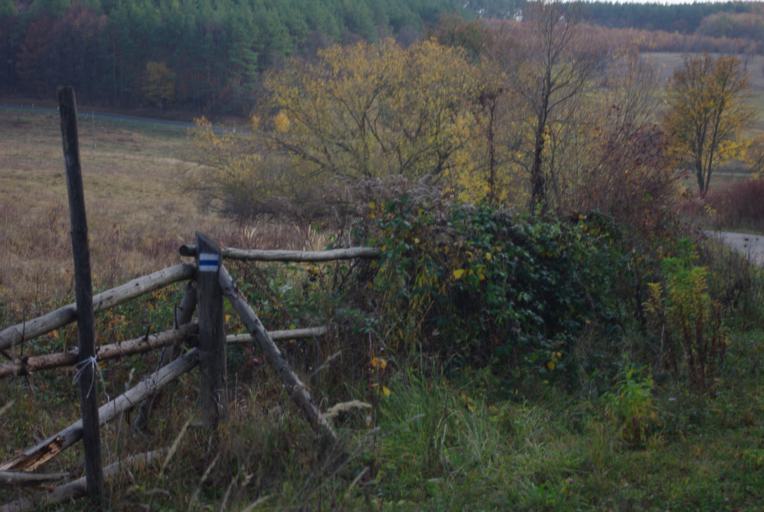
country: HU
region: Borsod-Abauj-Zemplen
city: Gonc
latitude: 48.5172
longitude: 21.4577
